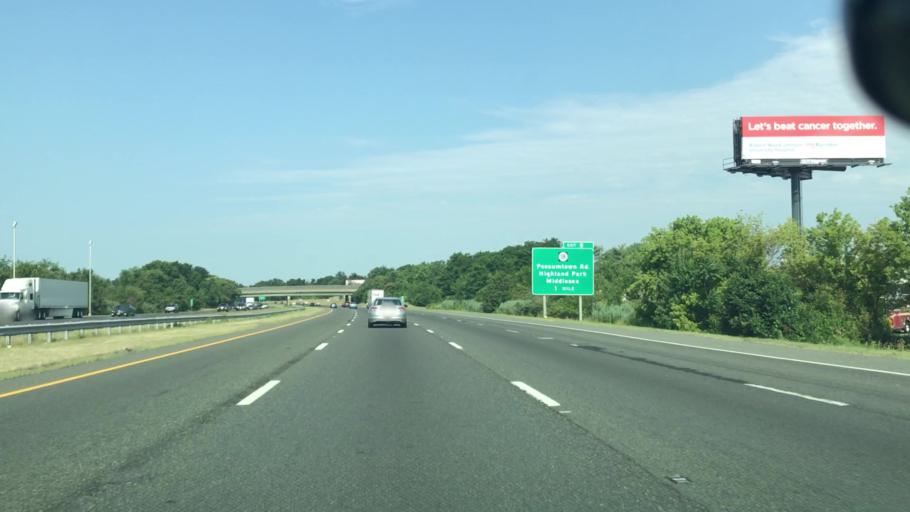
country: US
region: New Jersey
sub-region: Middlesex County
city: Society Hill
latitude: 40.5570
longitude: -74.4658
